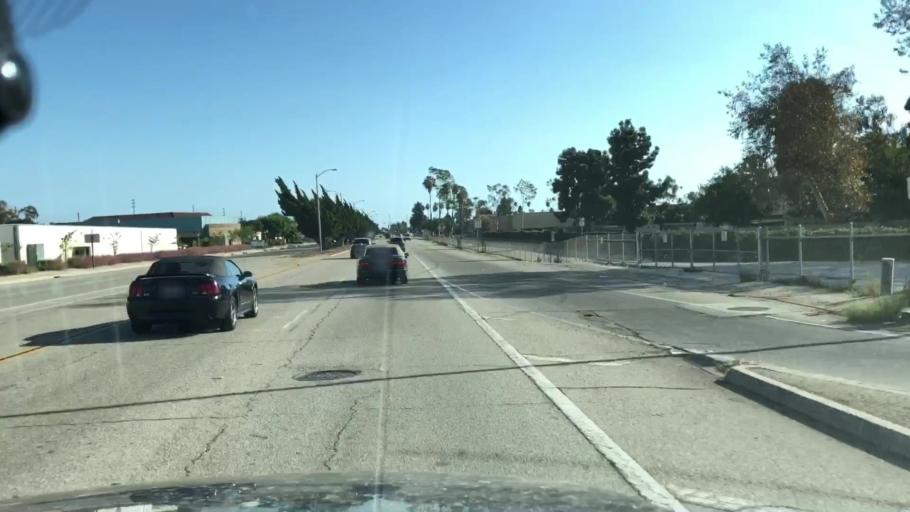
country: US
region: California
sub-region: Ventura County
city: El Rio
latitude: 34.2305
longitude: -119.1788
